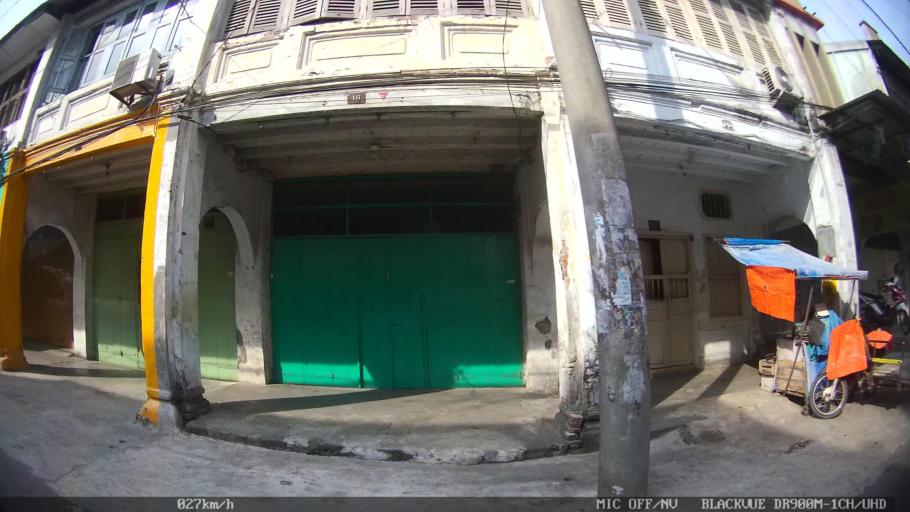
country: ID
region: North Sumatra
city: Binjai
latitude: 3.6089
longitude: 98.4916
